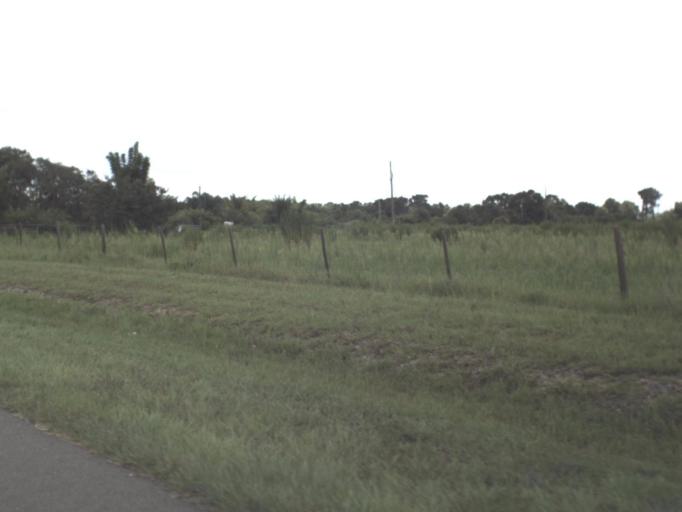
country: US
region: Florida
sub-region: Hillsborough County
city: Wimauma
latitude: 27.7106
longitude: -82.2699
